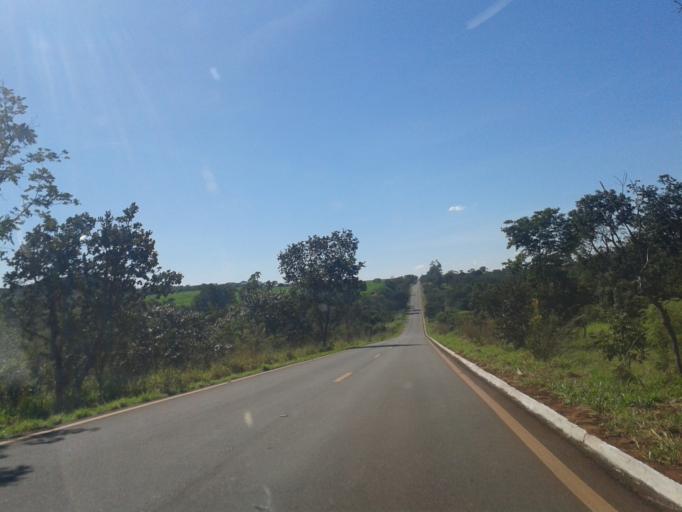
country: BR
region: Minas Gerais
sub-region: Ituiutaba
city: Ituiutaba
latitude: -19.1413
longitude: -49.7759
